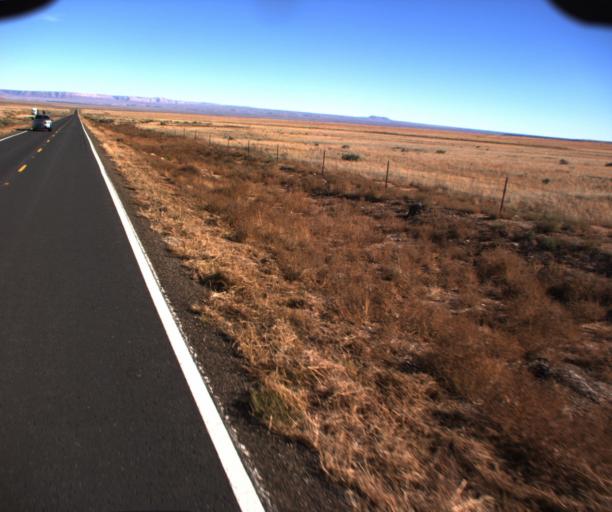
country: US
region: Arizona
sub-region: Coconino County
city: Fredonia
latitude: 36.7303
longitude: -112.0430
